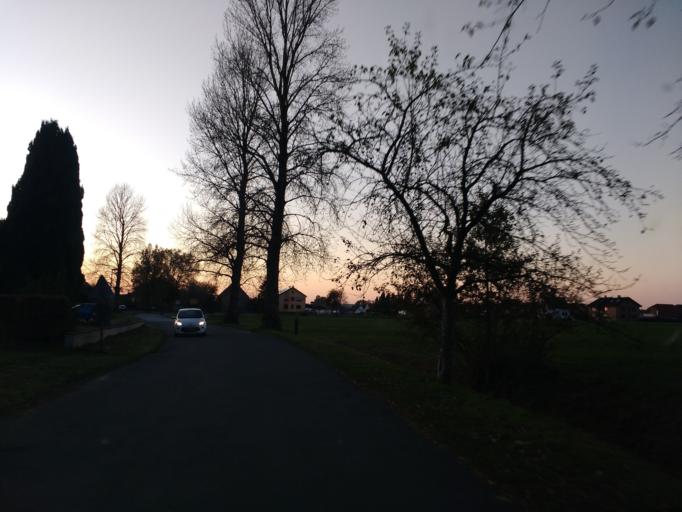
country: DE
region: North Rhine-Westphalia
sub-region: Regierungsbezirk Detmold
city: Schlangen
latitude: 51.7994
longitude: 8.8445
